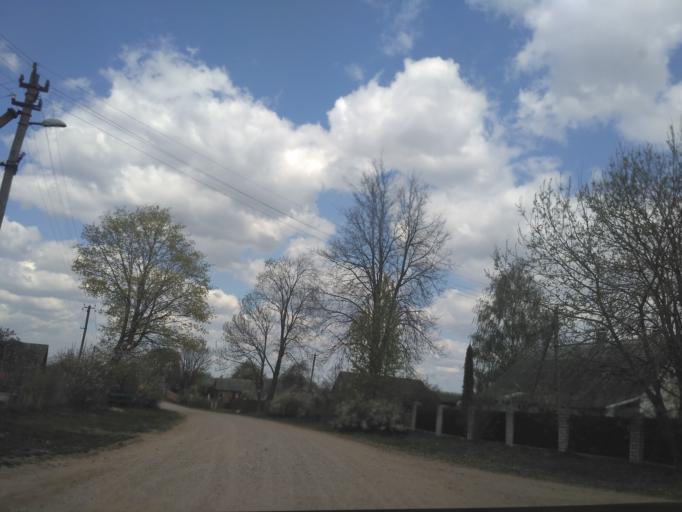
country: BY
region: Minsk
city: Radashkovichy
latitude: 54.2758
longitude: 27.3097
